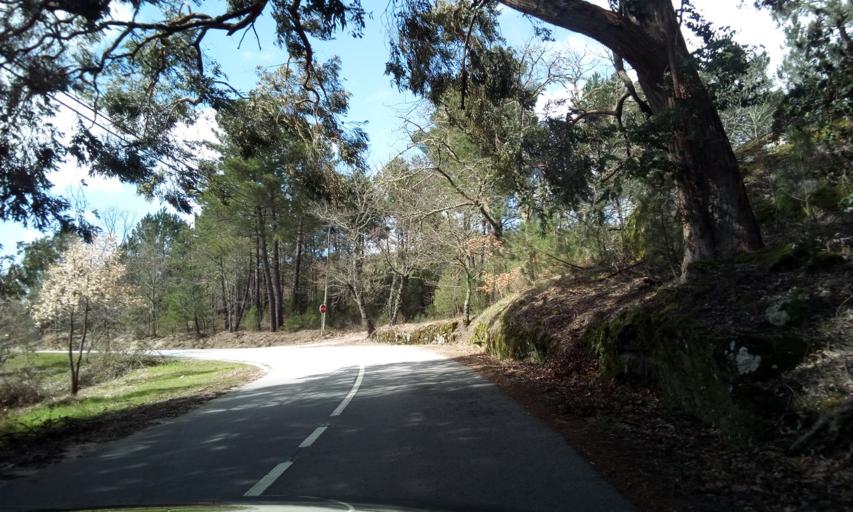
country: PT
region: Guarda
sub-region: Fornos de Algodres
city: Fornos de Algodres
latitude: 40.6331
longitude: -7.5460
